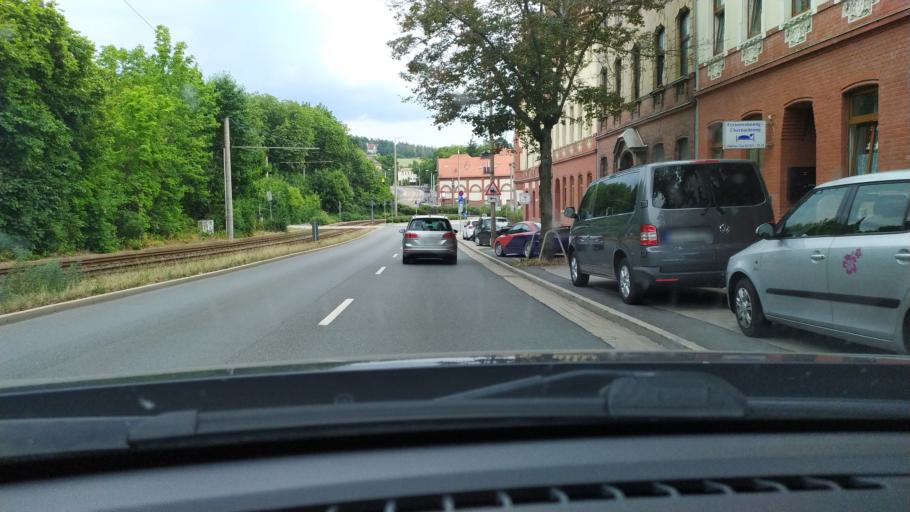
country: DE
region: Saxony
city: Plauen
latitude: 50.4946
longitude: 12.1534
